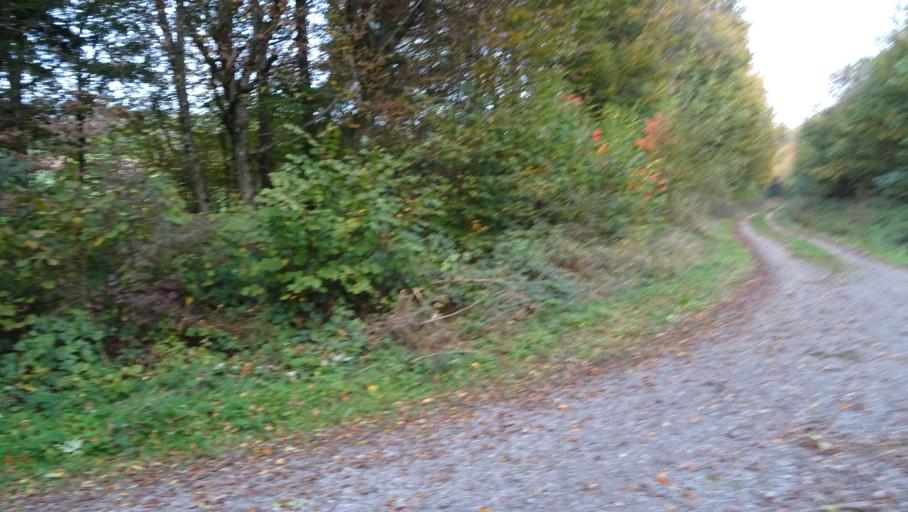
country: DE
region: Baden-Wuerttemberg
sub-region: Karlsruhe Region
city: Neckargerach
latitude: 49.3826
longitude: 9.0915
